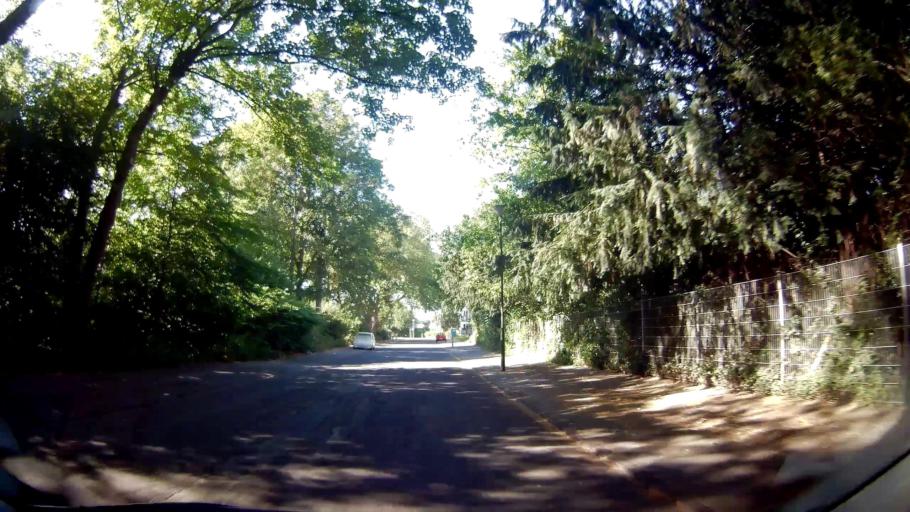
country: DE
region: North Rhine-Westphalia
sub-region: Regierungsbezirk Dusseldorf
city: Essen
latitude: 51.4704
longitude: 6.9985
